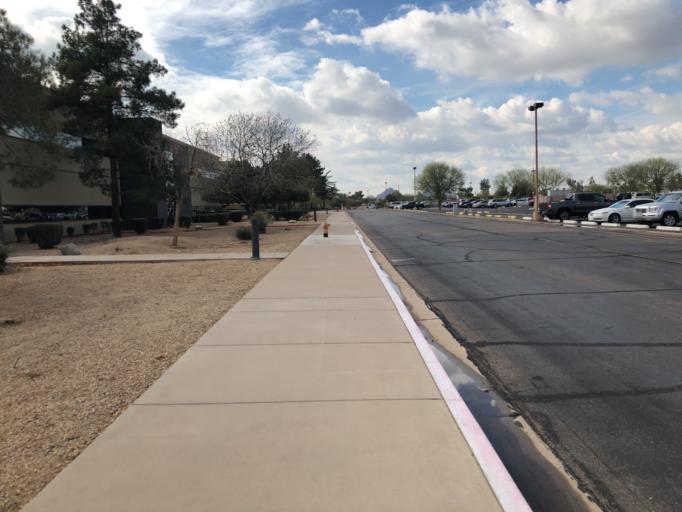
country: US
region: Arizona
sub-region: Maricopa County
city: Tempe
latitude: 33.4608
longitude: -111.9039
